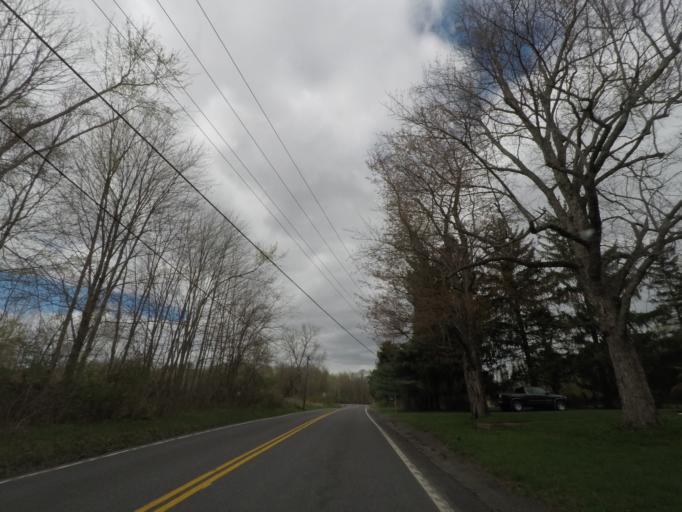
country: US
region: New York
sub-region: Columbia County
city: Chatham
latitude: 42.3206
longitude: -73.6234
